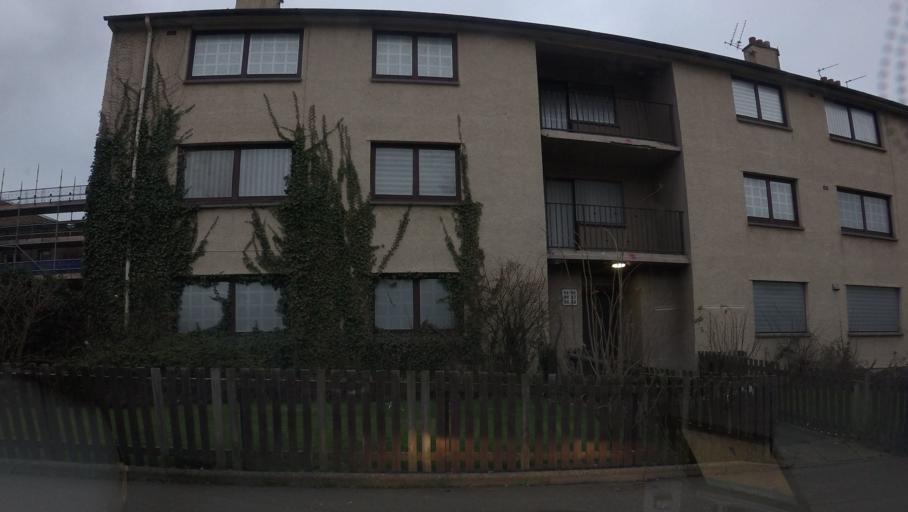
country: GB
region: Scotland
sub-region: Fife
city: Inverkeithing
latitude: 56.0316
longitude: -3.3888
